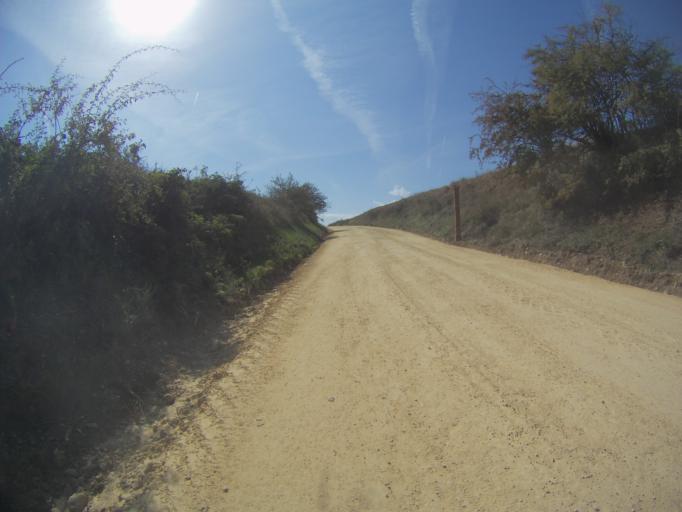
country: ES
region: La Rioja
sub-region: Provincia de La Rioja
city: Ciruena
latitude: 42.4236
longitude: -2.8777
